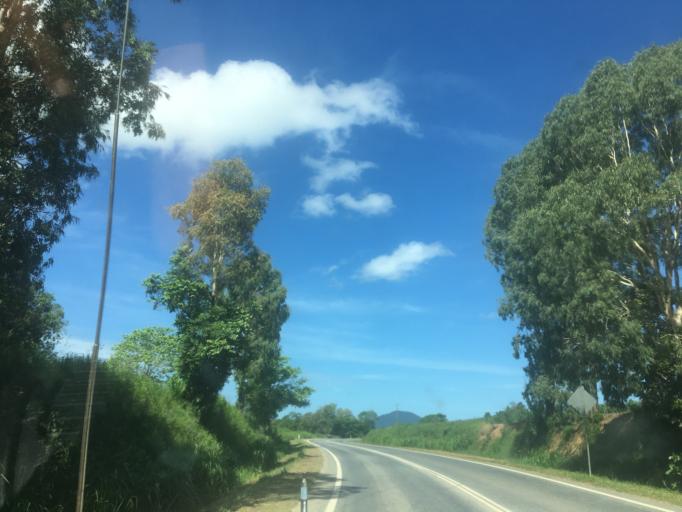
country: AU
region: Queensland
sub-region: Cairns
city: Woree
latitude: -17.0682
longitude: 145.7471
